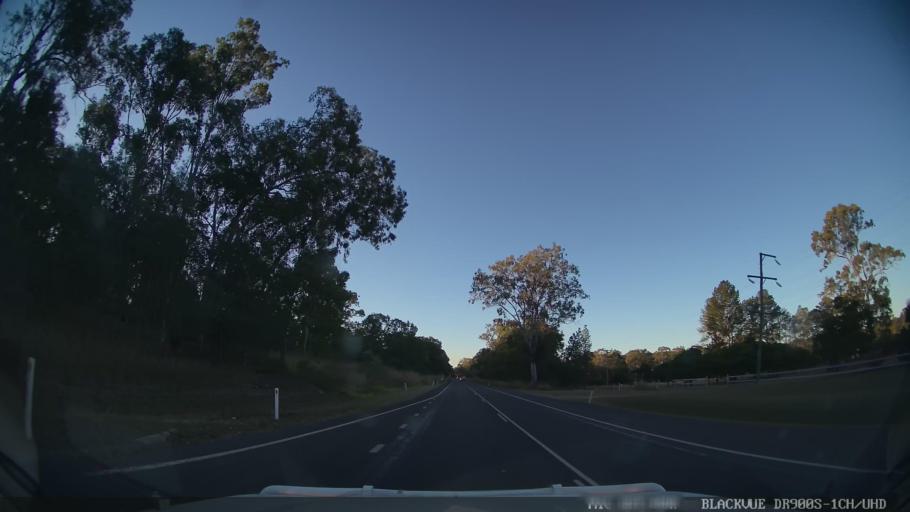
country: AU
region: Queensland
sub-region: Gladstone
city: Toolooa
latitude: -23.9601
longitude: 151.2186
